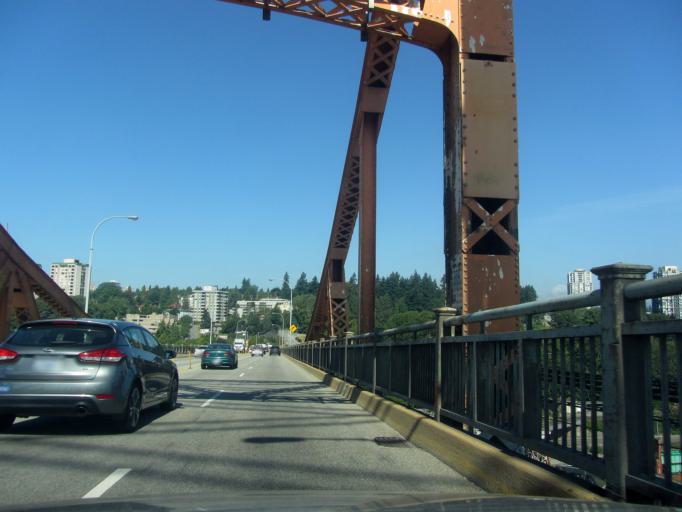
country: CA
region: British Columbia
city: New Westminster
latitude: 49.2080
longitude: -122.8953
